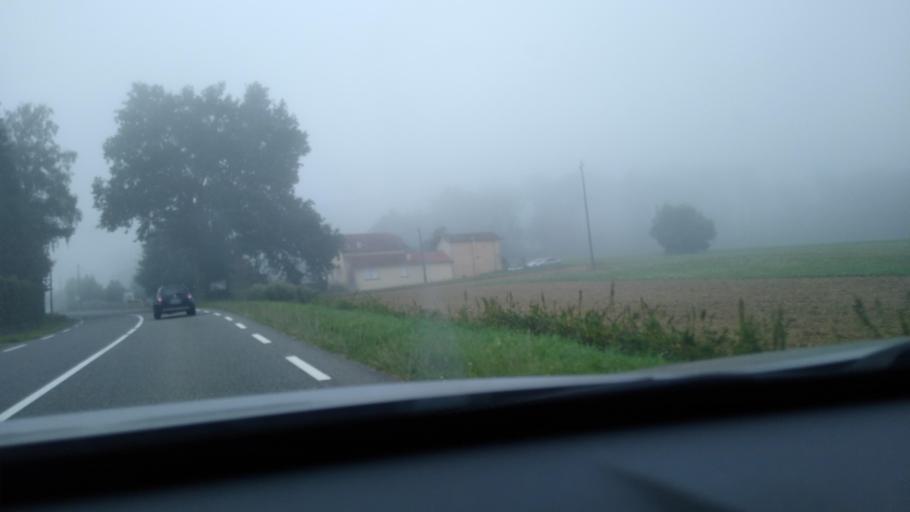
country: FR
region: Midi-Pyrenees
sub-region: Departement de la Haute-Garonne
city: Salies-du-Salat
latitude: 43.1076
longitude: 0.9386
